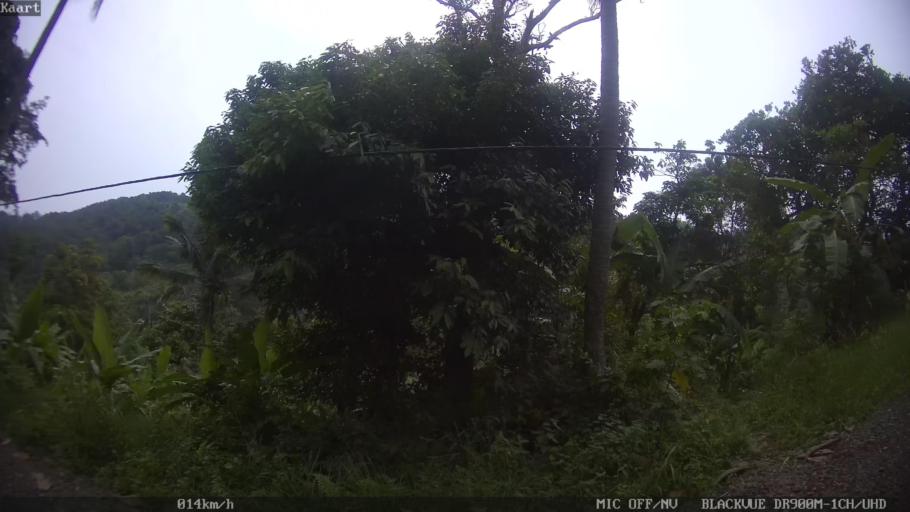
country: ID
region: Lampung
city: Panjang
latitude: -5.4281
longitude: 105.3094
